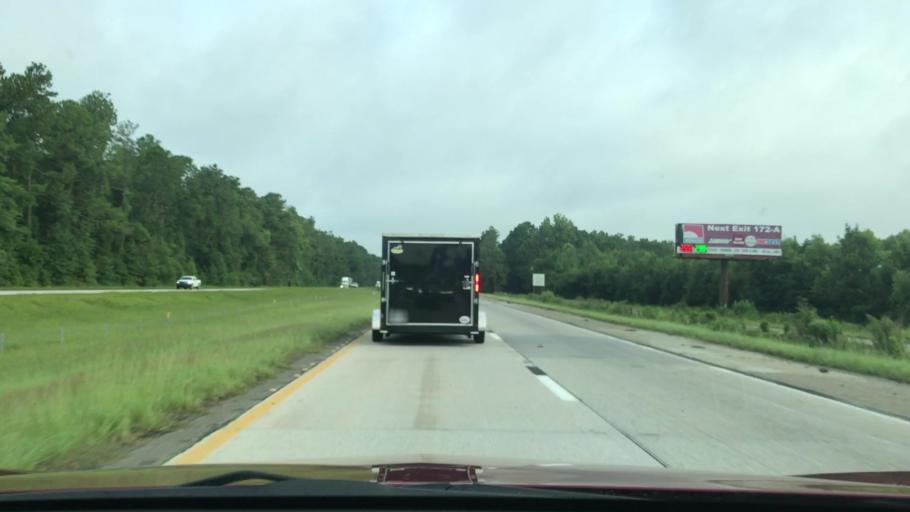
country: US
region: South Carolina
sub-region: Orangeburg County
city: Holly Hill
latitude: 33.2460
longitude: -80.4646
